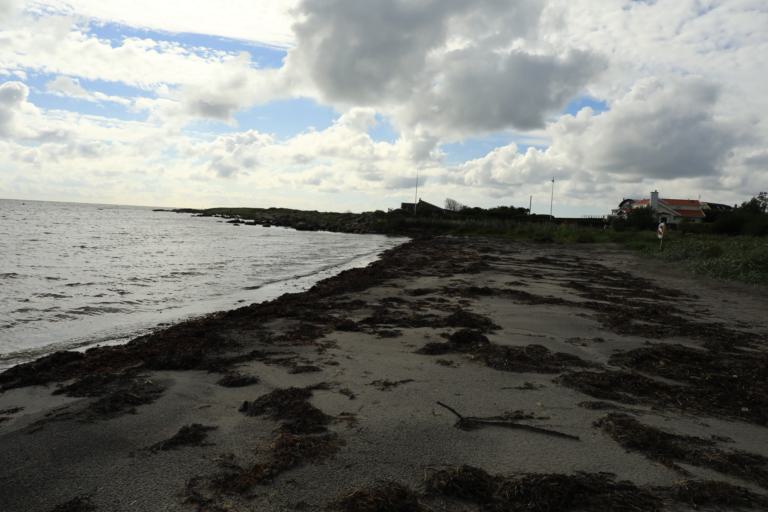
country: SE
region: Halland
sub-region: Varbergs Kommun
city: Traslovslage
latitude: 57.0665
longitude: 12.2594
